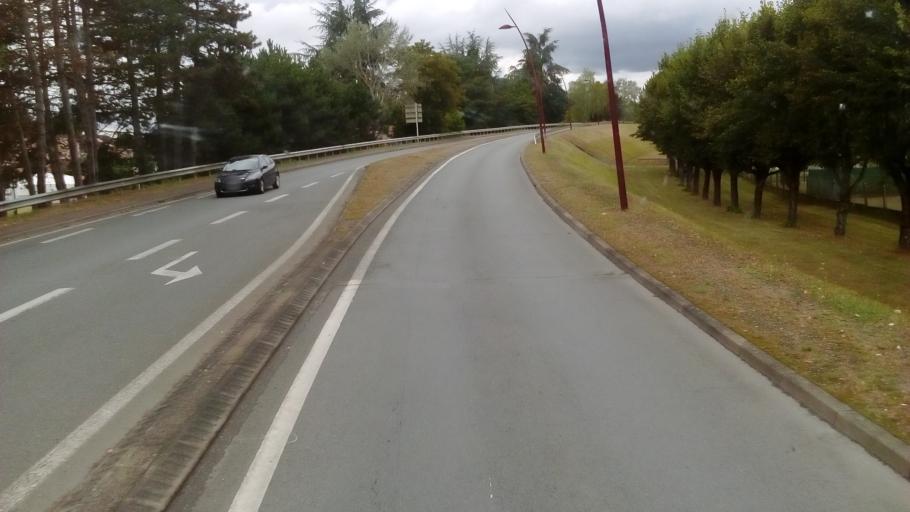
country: FR
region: Bourgogne
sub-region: Departement de Saone-et-Loire
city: Digoin
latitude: 46.4806
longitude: 3.9898
